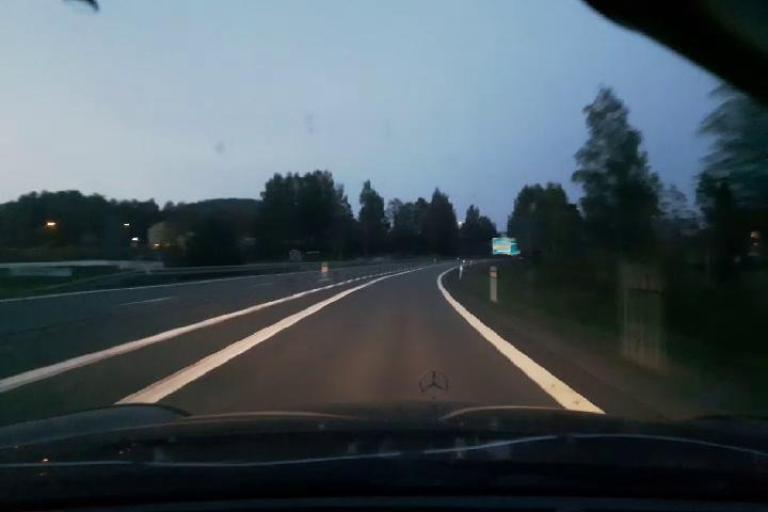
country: SE
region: Vaesternorrland
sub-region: Kramfors Kommun
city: Nordingra
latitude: 63.0562
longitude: 18.3347
